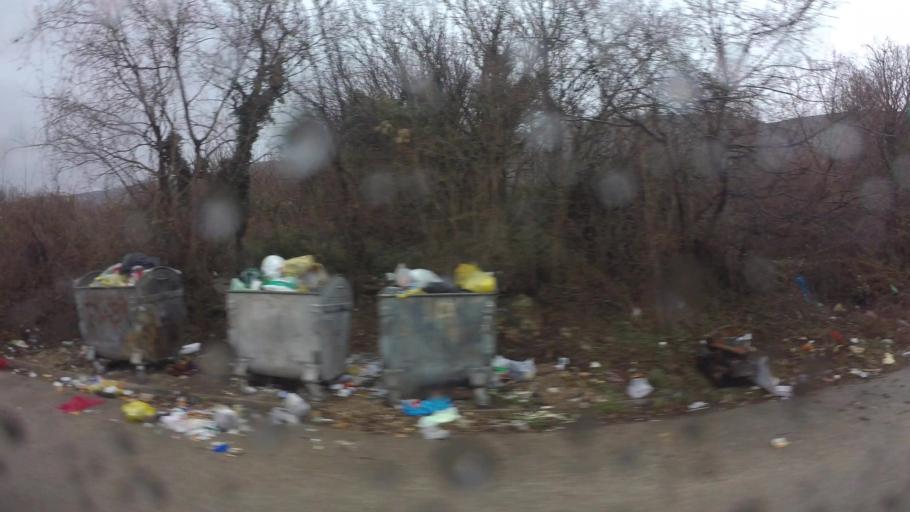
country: BA
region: Federation of Bosnia and Herzegovina
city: Rodoc
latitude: 43.3024
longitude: 17.8537
